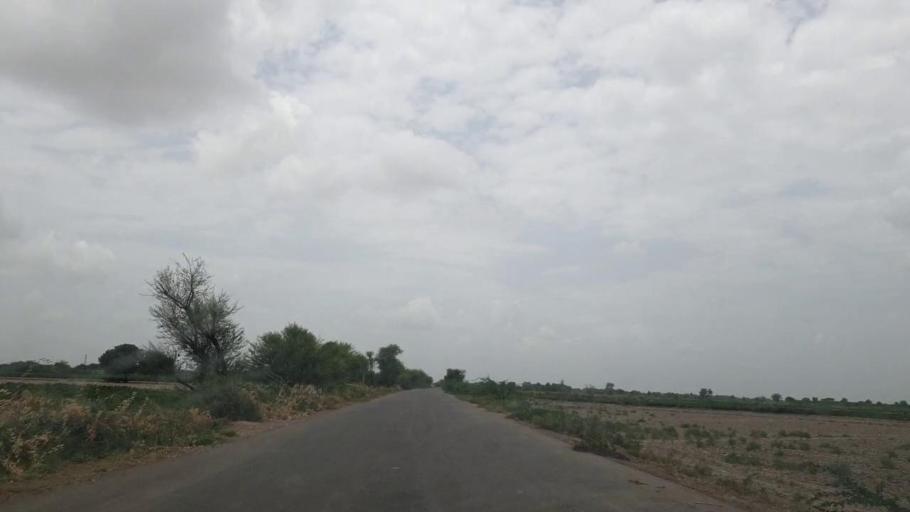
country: PK
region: Sindh
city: Naukot
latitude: 24.8943
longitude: 69.2558
